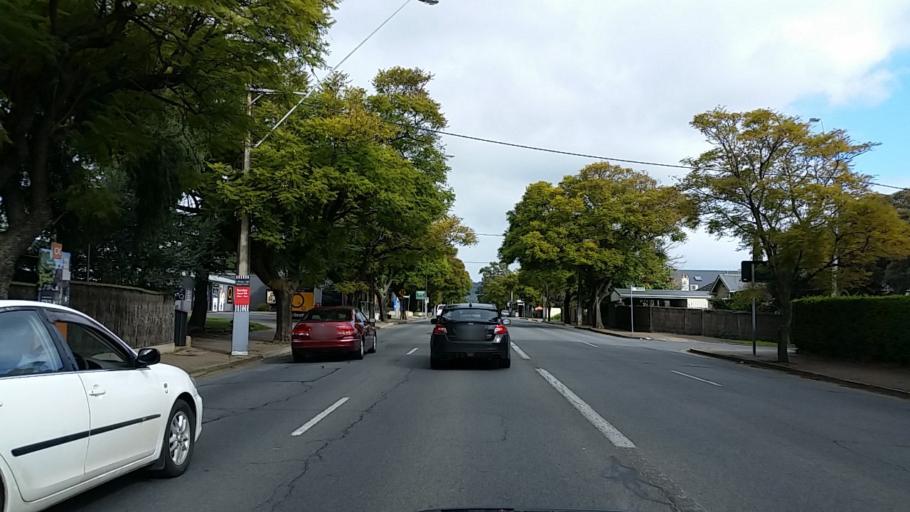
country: AU
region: South Australia
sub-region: Unley
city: Fullarton
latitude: -34.9545
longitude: 138.6257
